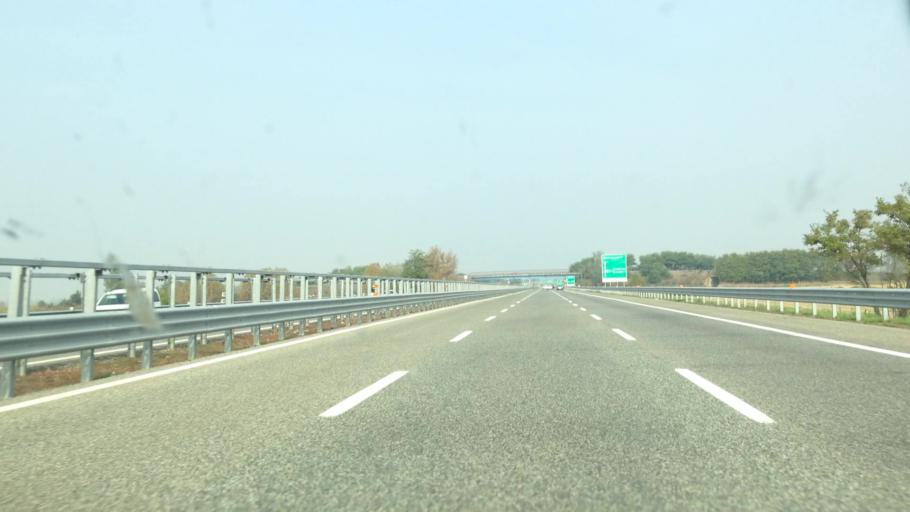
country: IT
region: Piedmont
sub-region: Provincia di Vercelli
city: Stroppiana
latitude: 45.2297
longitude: 8.4737
